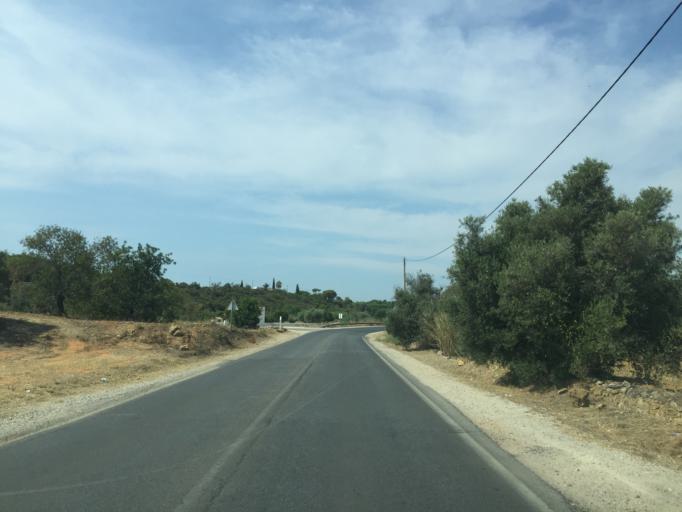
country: PT
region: Faro
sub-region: Loule
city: Quarteira
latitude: 37.0729
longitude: -8.0681
